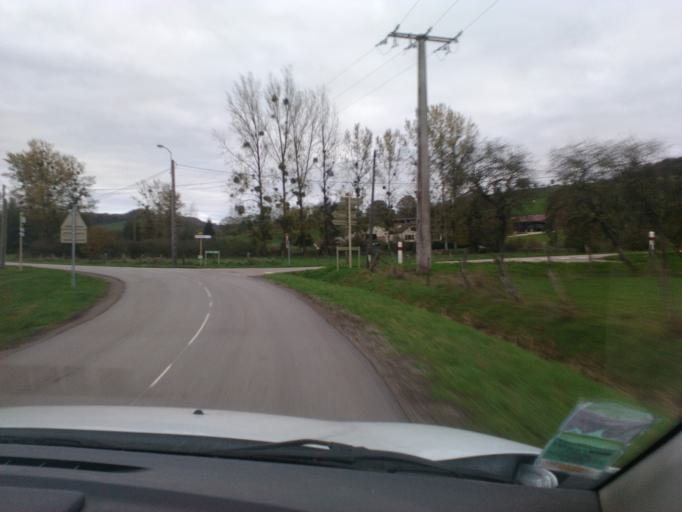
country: FR
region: Lorraine
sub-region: Departement des Vosges
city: Vincey
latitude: 48.2681
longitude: 6.2640
